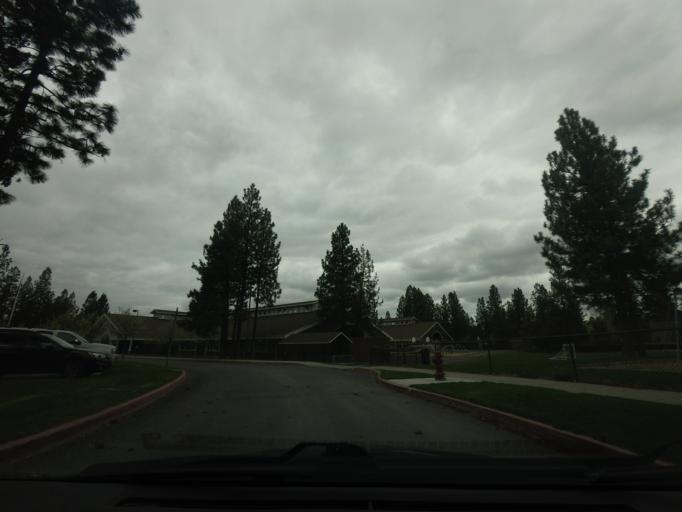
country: US
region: Oregon
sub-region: Deschutes County
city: Bend
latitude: 44.0236
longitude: -121.3304
